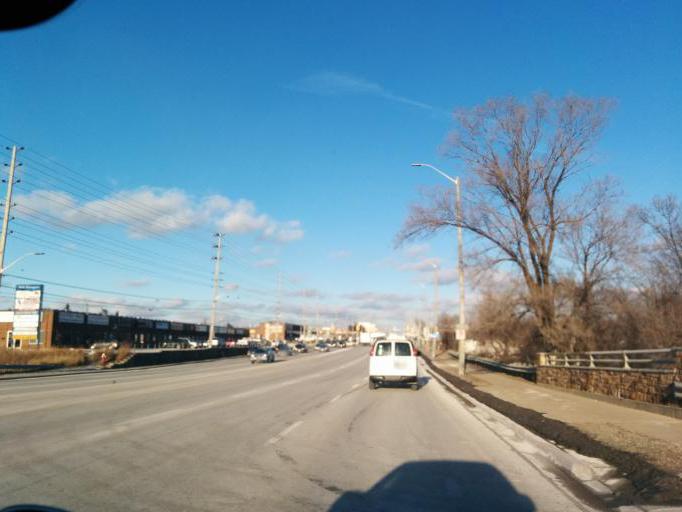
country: CA
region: Ontario
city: Mississauga
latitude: 43.6285
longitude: -79.6286
